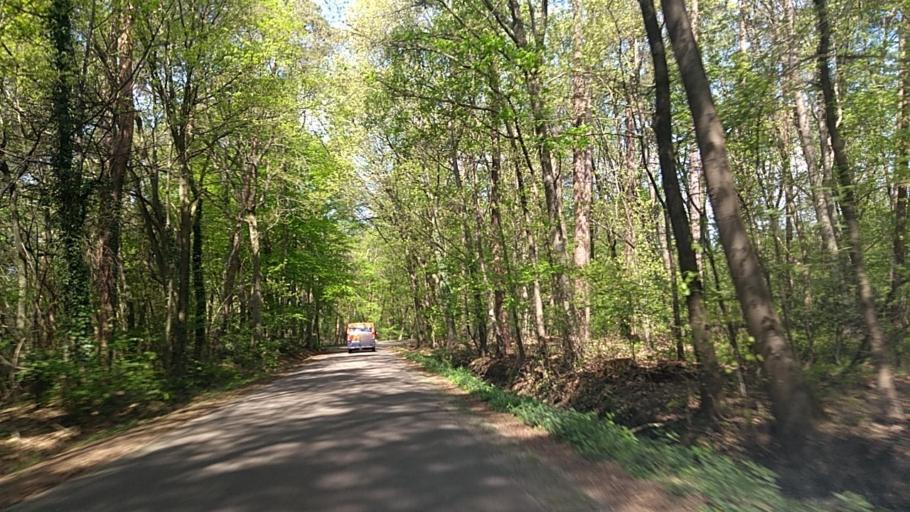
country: NL
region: Overijssel
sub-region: Gemeente Haaksbergen
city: Haaksbergen
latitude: 52.1351
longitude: 6.7233
